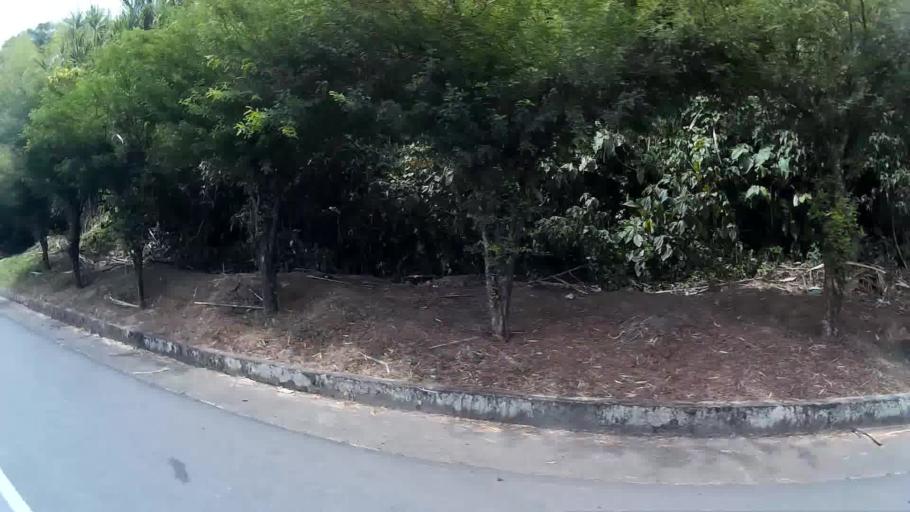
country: CO
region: Risaralda
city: Pereira
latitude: 4.8119
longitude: -75.7511
